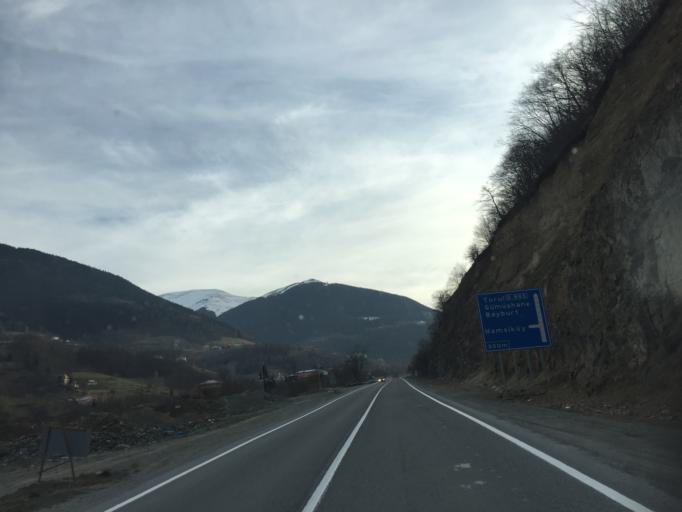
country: TR
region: Trabzon
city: Macka
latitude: 40.7226
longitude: 39.5192
